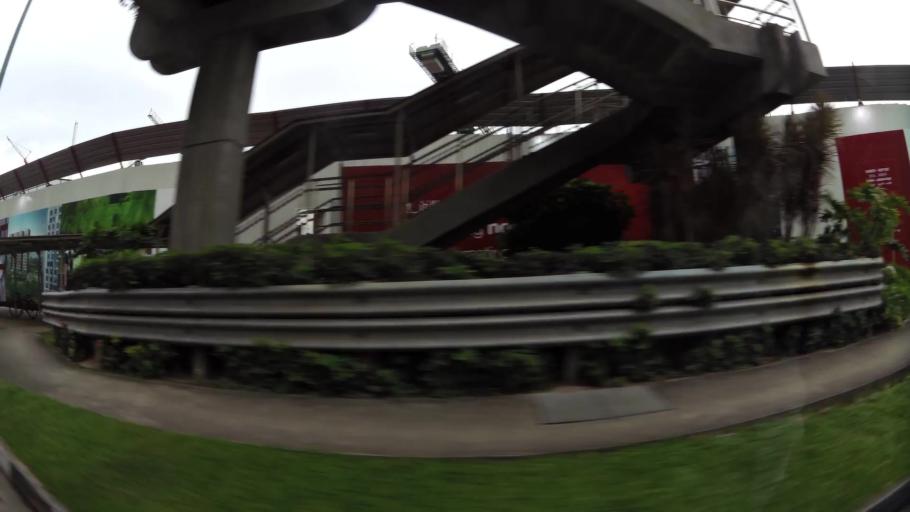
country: SG
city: Singapore
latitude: 1.3356
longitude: 103.8705
